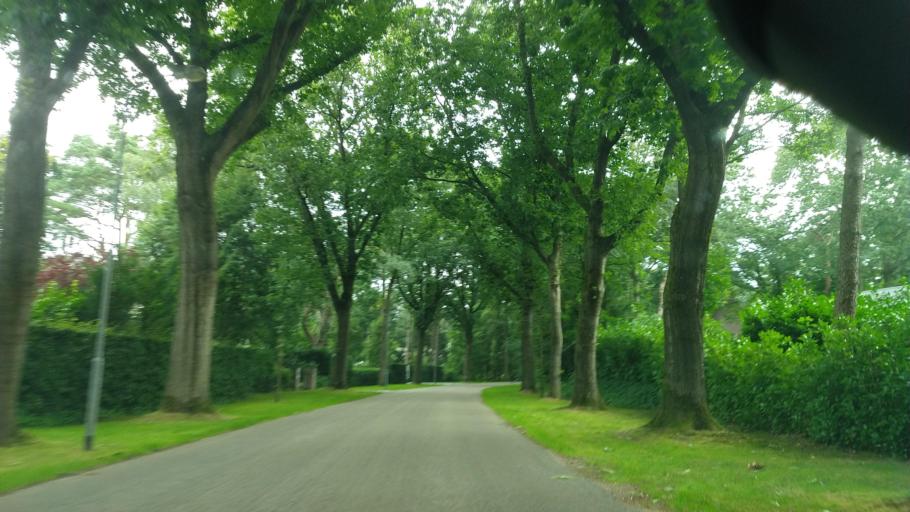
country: NL
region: Gelderland
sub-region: Gemeente Ermelo
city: Ermelo
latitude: 52.3061
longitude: 5.6253
